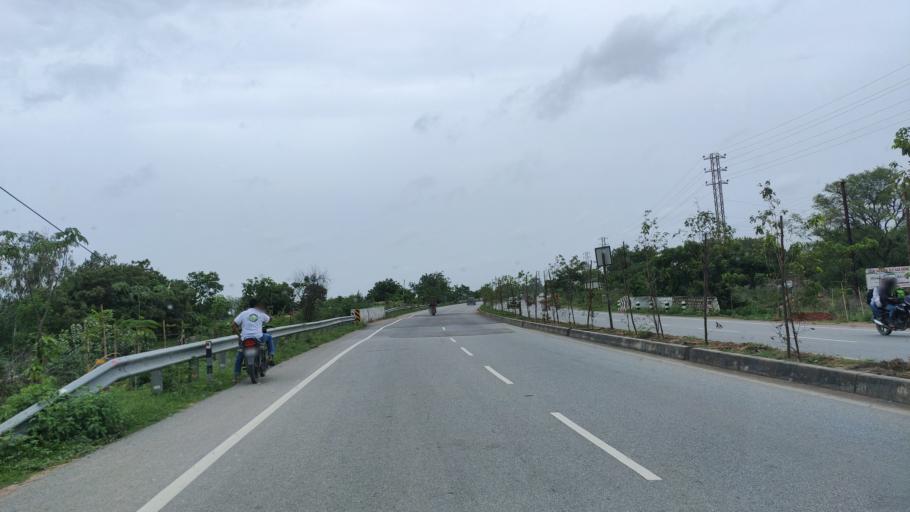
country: IN
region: Telangana
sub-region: Rangareddi
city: Secunderabad
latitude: 17.6019
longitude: 78.5676
